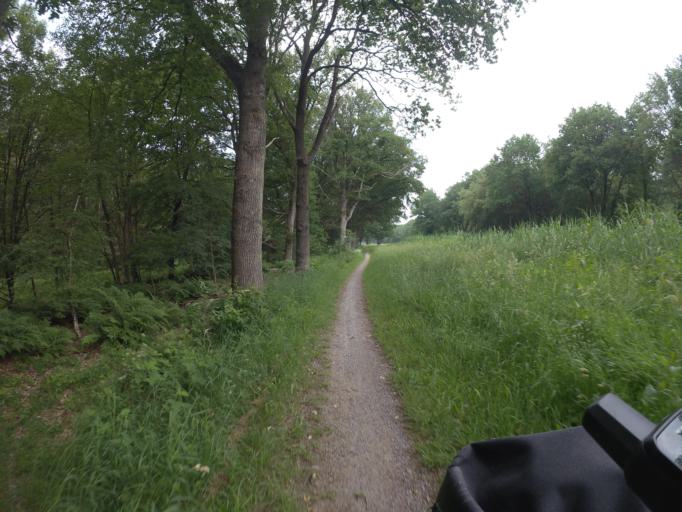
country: NL
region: Drenthe
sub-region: Gemeente Assen
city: Assen
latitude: 53.0143
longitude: 6.4246
